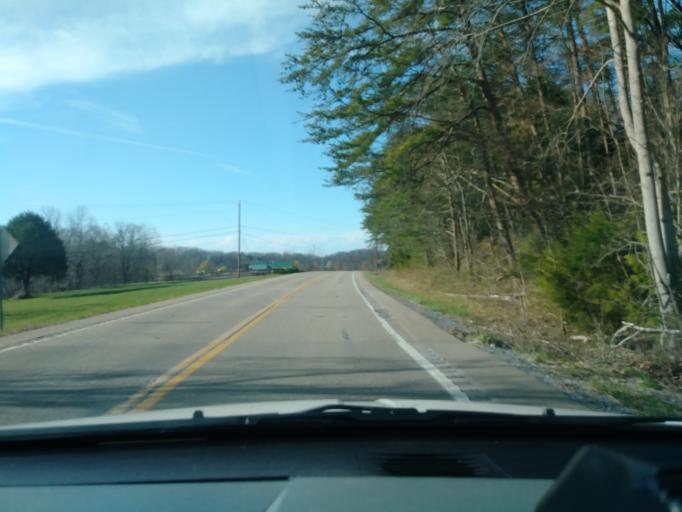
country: US
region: Tennessee
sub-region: Greene County
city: Greeneville
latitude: 35.9999
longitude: -82.8314
